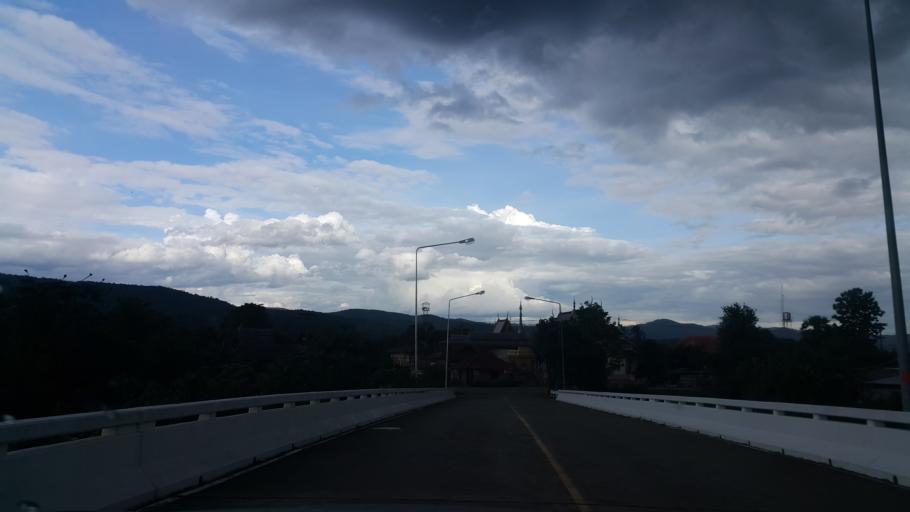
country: TH
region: Chiang Mai
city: Mae Taeng
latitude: 19.0765
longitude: 98.9510
